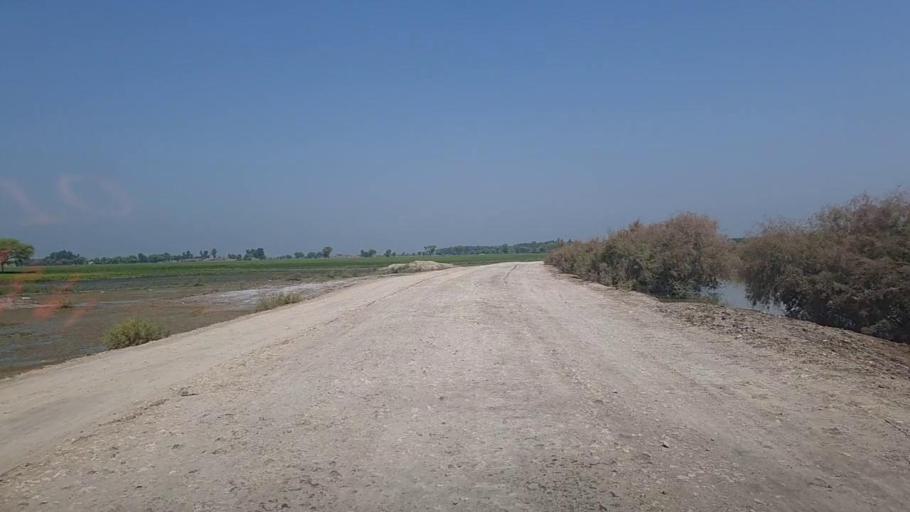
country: PK
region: Sindh
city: Kandhkot
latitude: 28.2999
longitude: 69.2909
